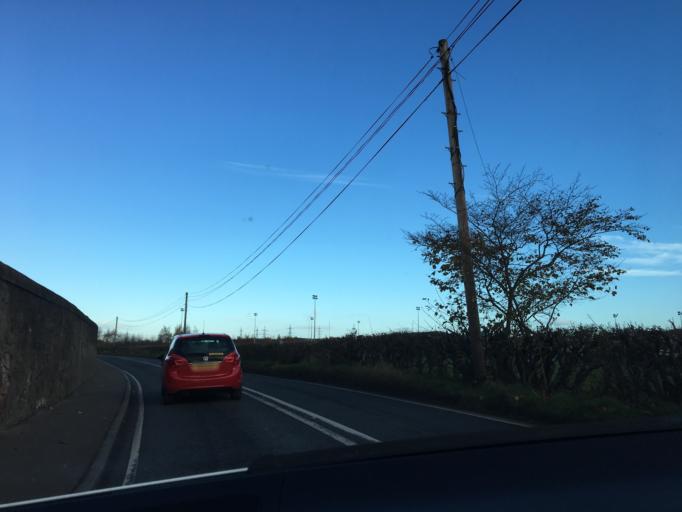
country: GB
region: Scotland
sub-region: Midlothian
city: Dalkeith
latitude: 55.9010
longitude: -3.0514
